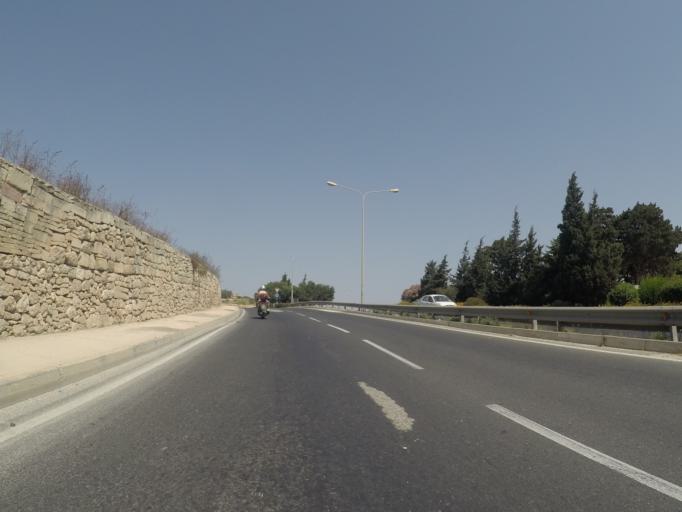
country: MT
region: L-Imdina
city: Imdina
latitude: 35.8903
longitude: 14.4095
